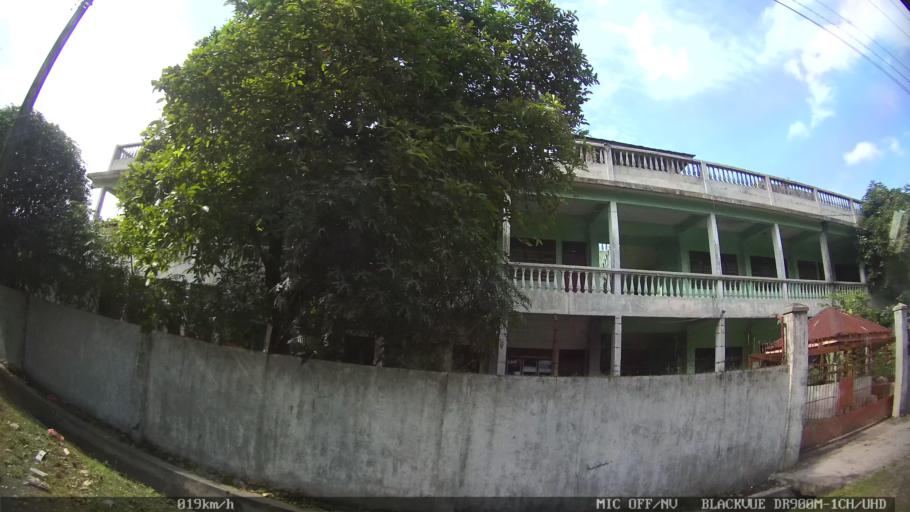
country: ID
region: North Sumatra
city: Medan
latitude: 3.6151
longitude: 98.6588
